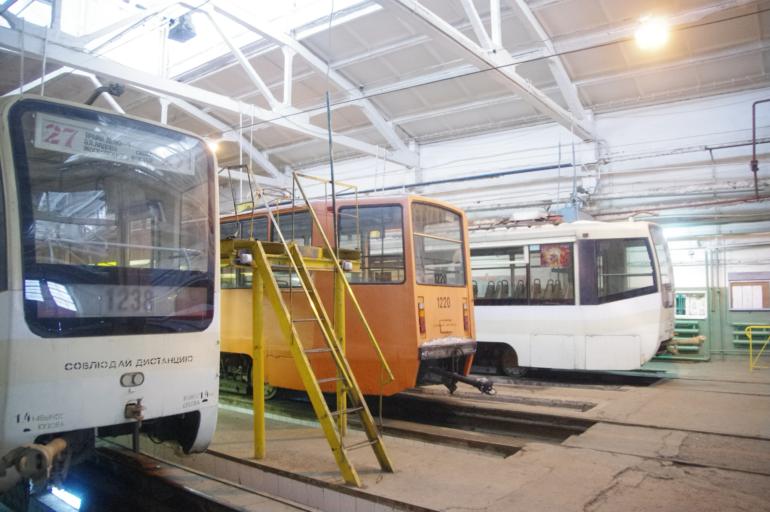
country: RU
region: Nizjnij Novgorod
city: Nizhniy Novgorod
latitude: 56.3011
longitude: 44.0491
